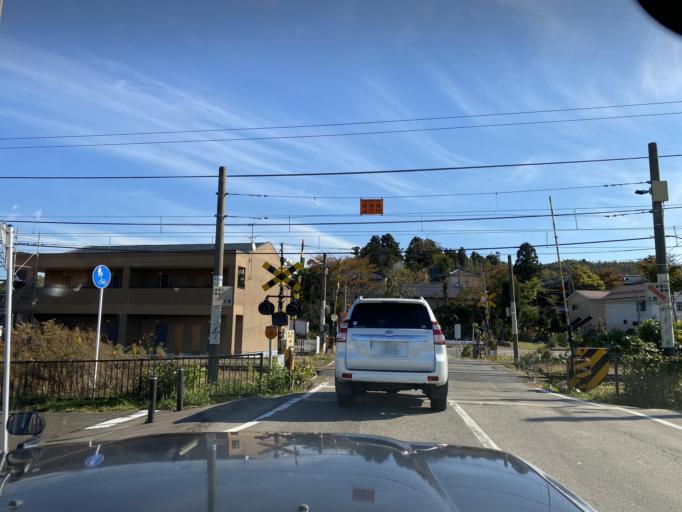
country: JP
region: Niigata
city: Niitsu-honcho
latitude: 37.7531
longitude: 139.0983
